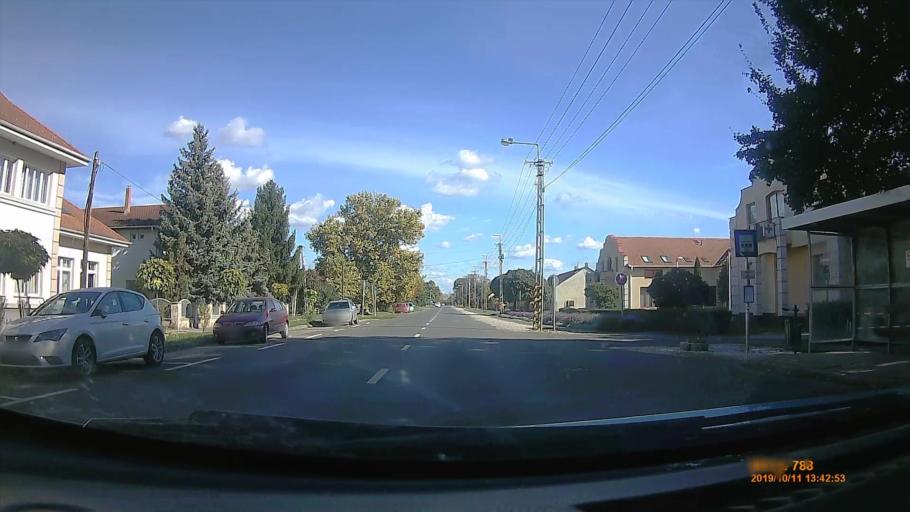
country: HU
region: Hajdu-Bihar
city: Balmazujvaros
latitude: 47.5391
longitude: 21.3470
